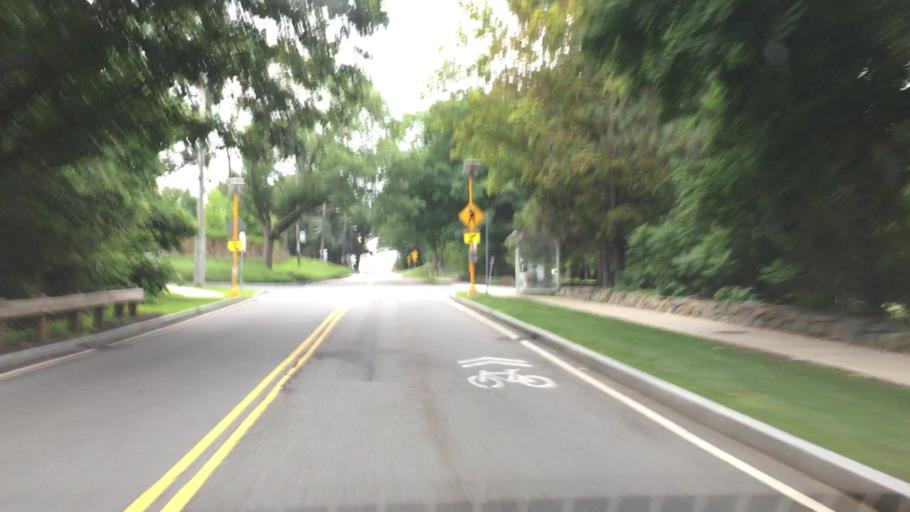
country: US
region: Massachusetts
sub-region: Middlesex County
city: Waltham
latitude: 42.4073
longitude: -71.2565
